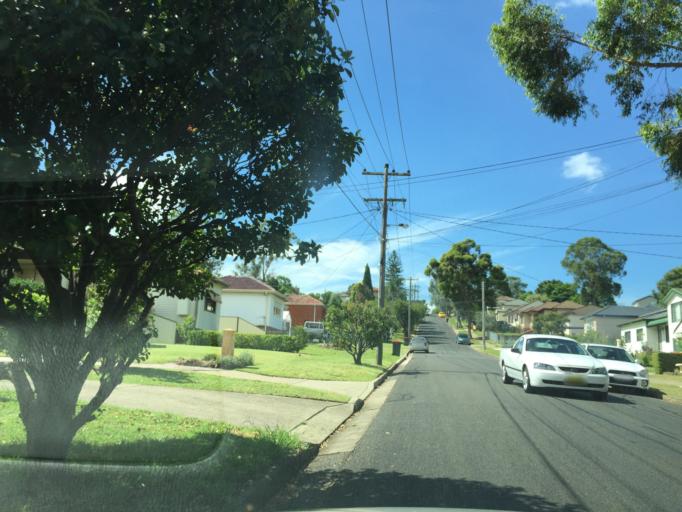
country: AU
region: New South Wales
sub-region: Blacktown
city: Doonside
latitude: -33.7812
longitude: 150.8900
